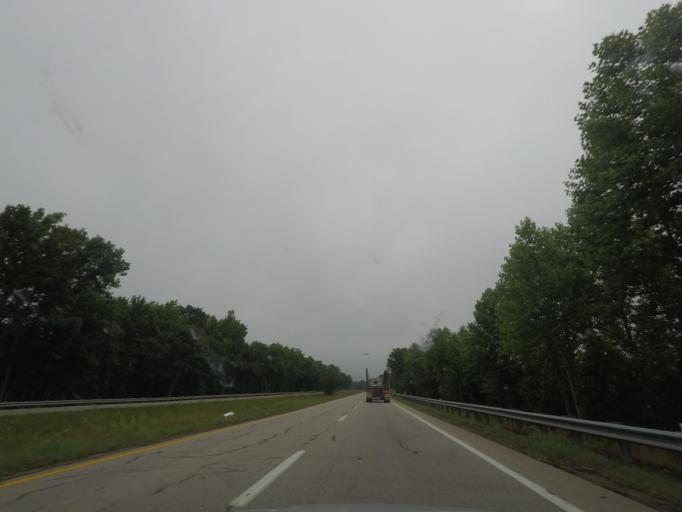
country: US
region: Virginia
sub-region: Charlotte County
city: Charlotte Court House
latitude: 37.0262
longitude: -78.4731
